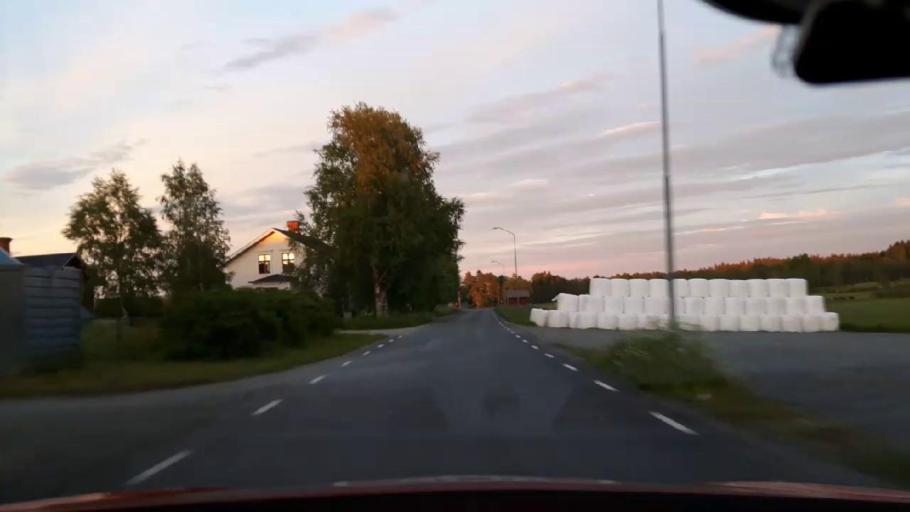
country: SE
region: Jaemtland
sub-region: OEstersunds Kommun
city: Brunflo
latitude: 63.0563
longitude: 14.8146
